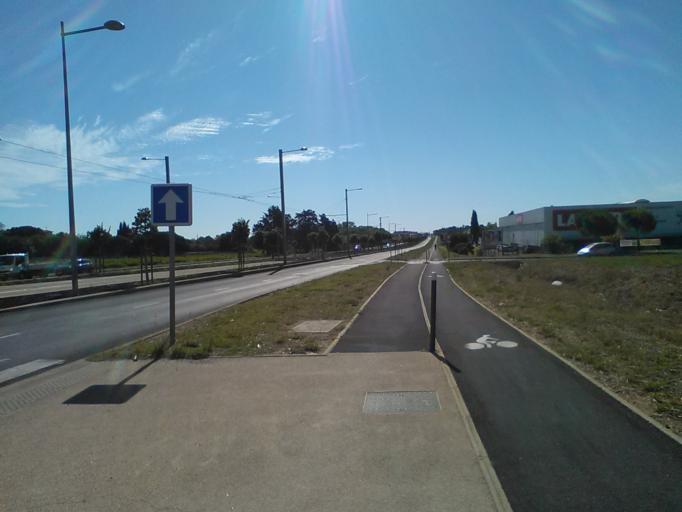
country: FR
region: Languedoc-Roussillon
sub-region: Departement de l'Herault
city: Perols
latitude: 43.5776
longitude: 3.9357
